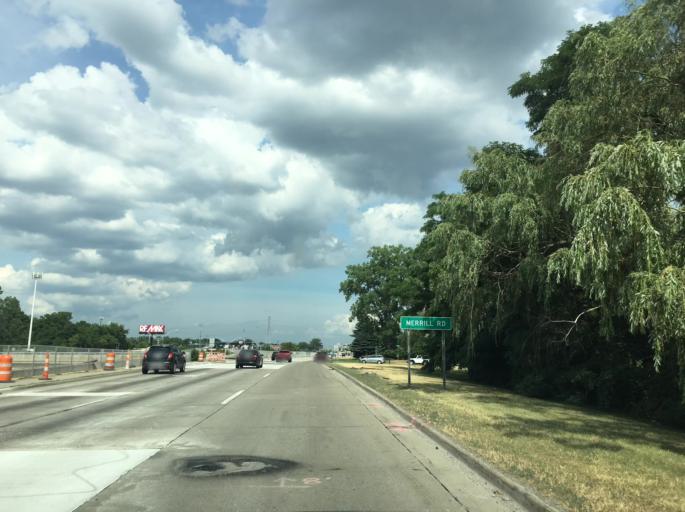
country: US
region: Michigan
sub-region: Macomb County
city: Utica
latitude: 42.6244
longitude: -83.0483
